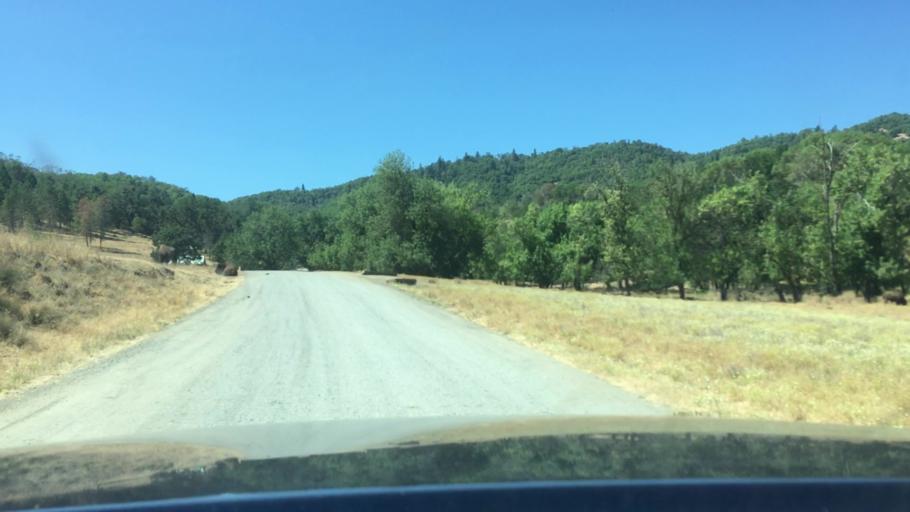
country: US
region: Oregon
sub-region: Douglas County
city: Winston
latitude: 43.1315
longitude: -123.4355
